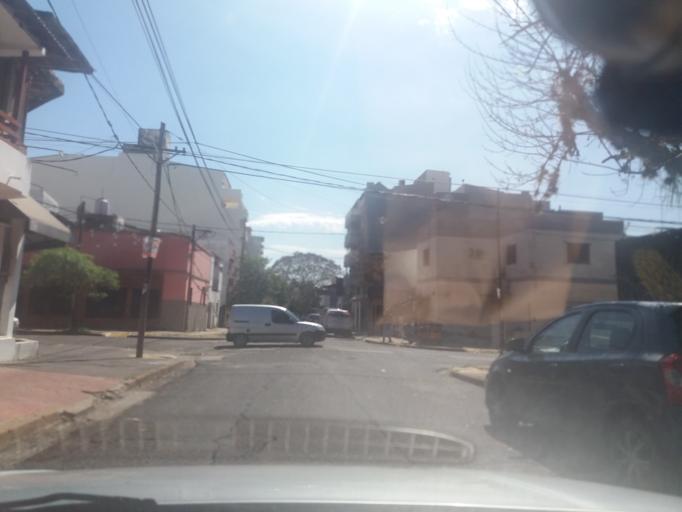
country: AR
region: Corrientes
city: Corrientes
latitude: -27.4682
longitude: -58.8456
